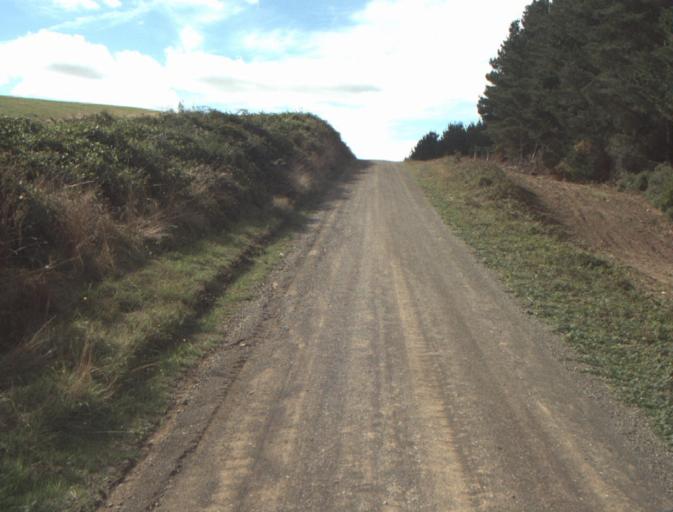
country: AU
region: Tasmania
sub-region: Launceston
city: Mayfield
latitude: -41.1864
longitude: 147.1783
